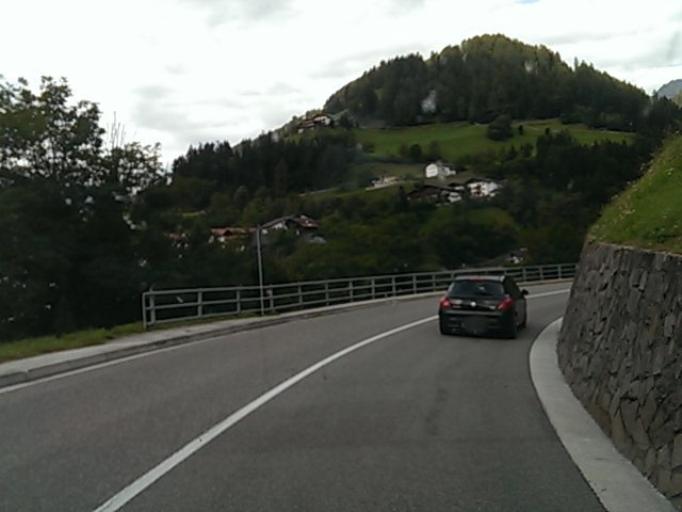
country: IT
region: Trentino-Alto Adige
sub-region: Bolzano
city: San Pancrazio
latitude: 46.5885
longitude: 11.0887
